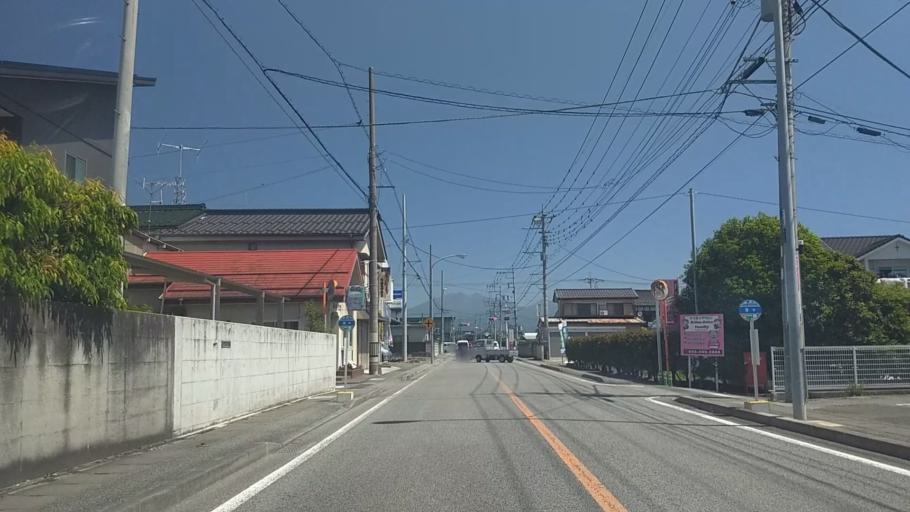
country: JP
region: Yamanashi
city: Ryuo
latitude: 35.6548
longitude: 138.4640
